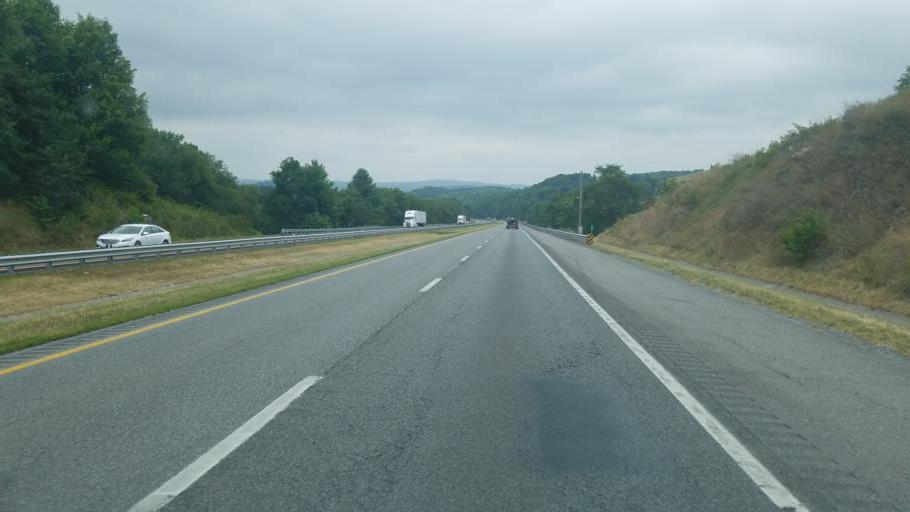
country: US
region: Virginia
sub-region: Bland County
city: Bland
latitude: 37.0558
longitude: -81.1334
